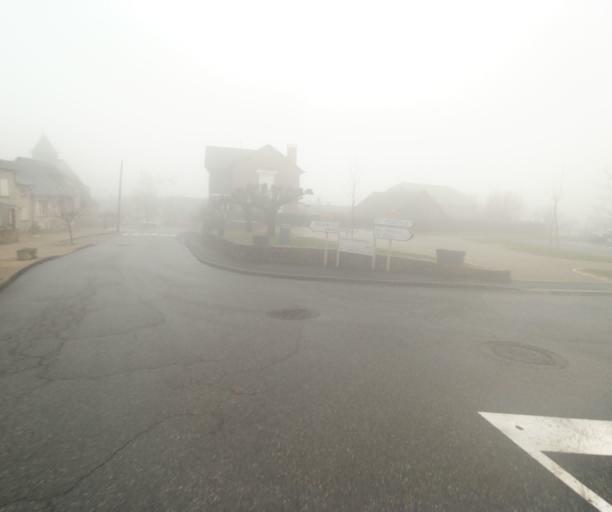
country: FR
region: Limousin
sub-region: Departement de la Correze
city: Sainte-Fereole
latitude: 45.1952
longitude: 1.6234
